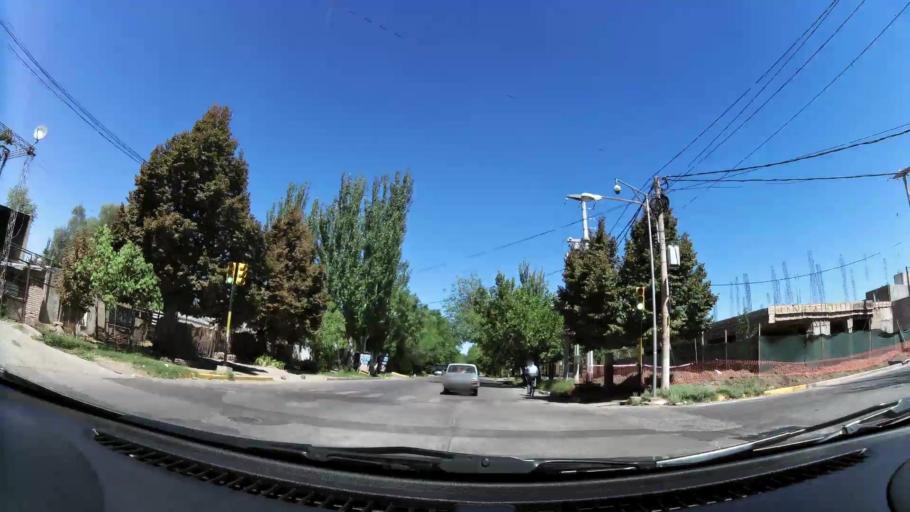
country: AR
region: Mendoza
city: Las Heras
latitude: -32.8463
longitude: -68.8467
